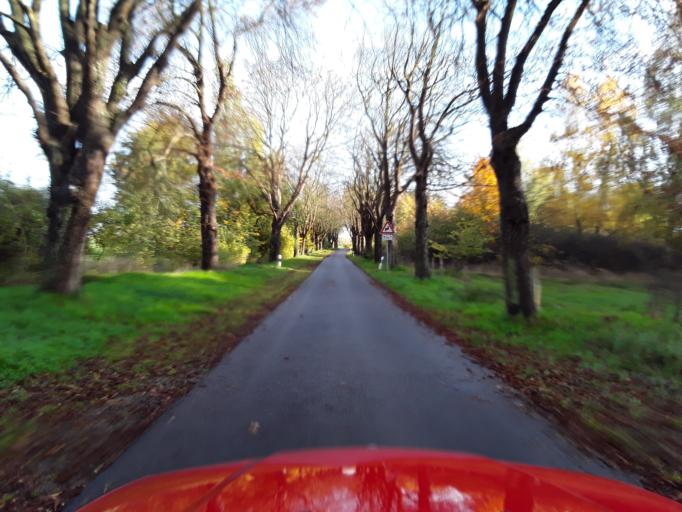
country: DE
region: Brandenburg
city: Mittenwalde
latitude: 53.2662
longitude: 13.7120
